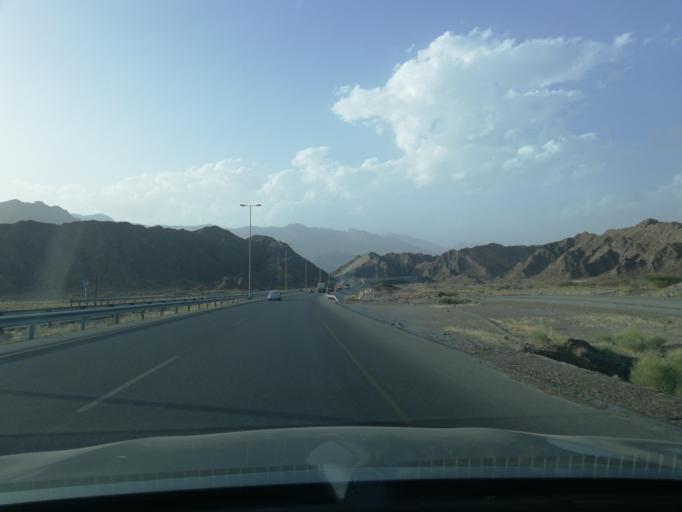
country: OM
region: Muhafazat ad Dakhiliyah
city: Izki
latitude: 22.9529
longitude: 57.7881
